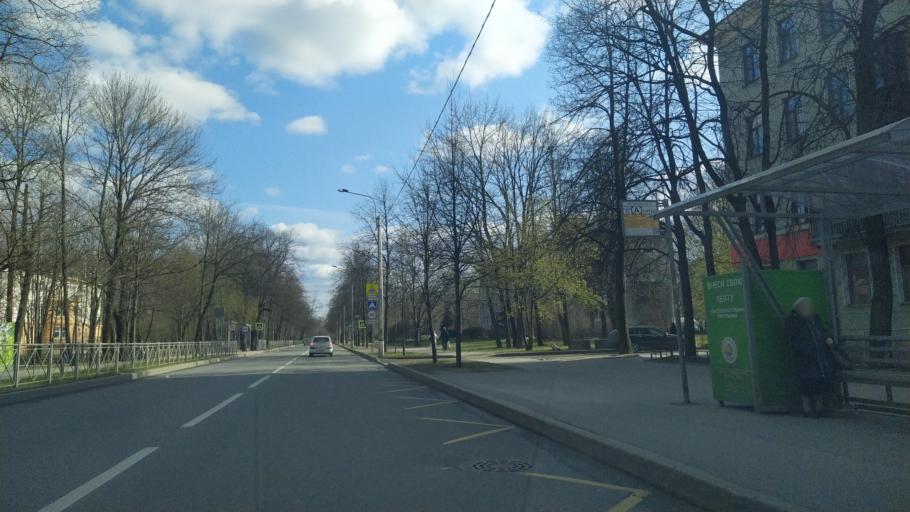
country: RU
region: St.-Petersburg
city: Pushkin
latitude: 59.7073
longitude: 30.4159
